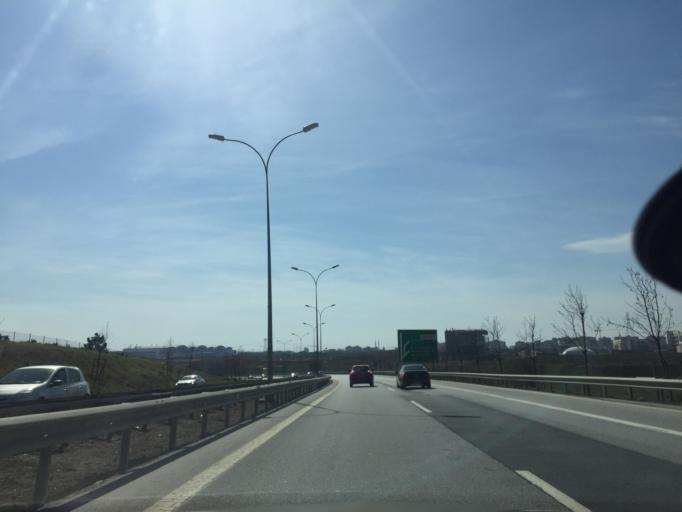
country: TR
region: Istanbul
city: Sultanbeyli
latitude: 40.9234
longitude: 29.3235
